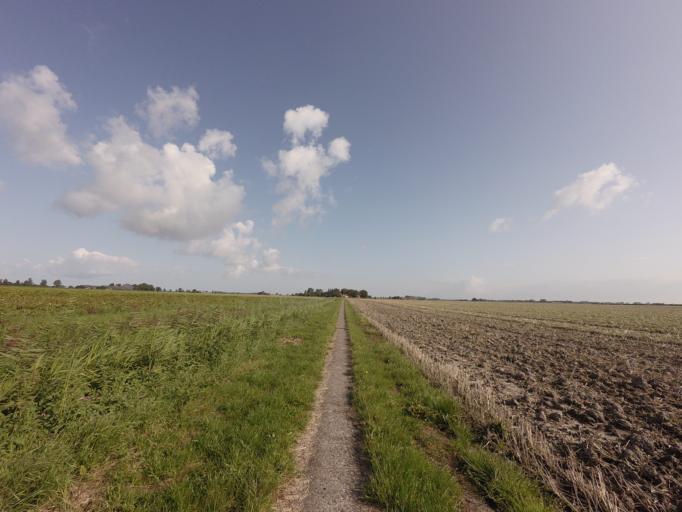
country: NL
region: Friesland
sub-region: Gemeente Franekeradeel
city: Franeker
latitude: 53.2054
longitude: 5.5646
